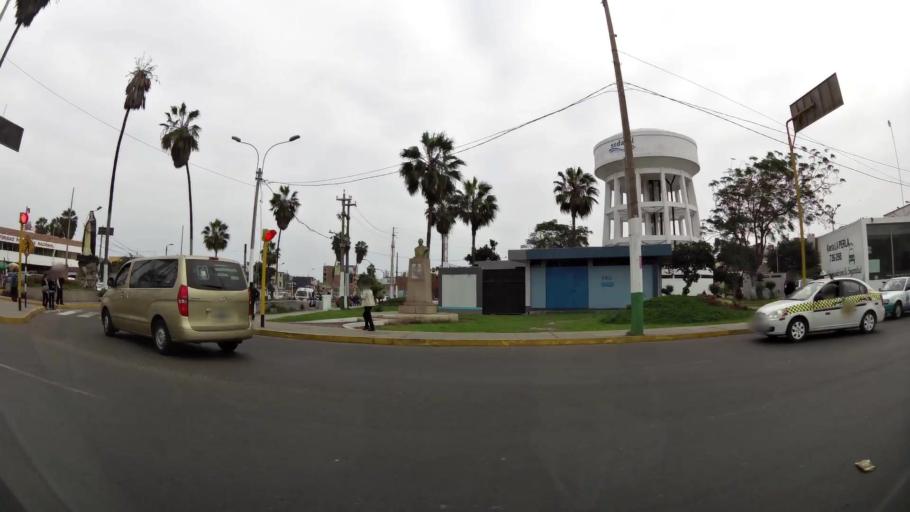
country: PE
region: Callao
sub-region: Callao
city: Callao
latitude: -12.0657
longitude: -77.1196
